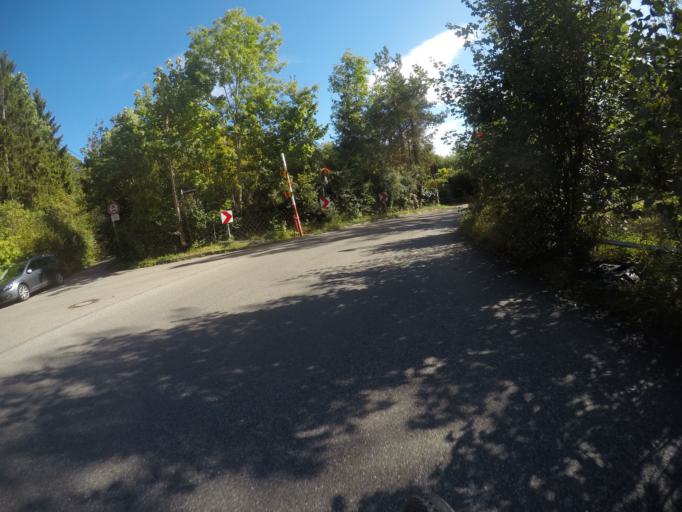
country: DE
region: Baden-Wuerttemberg
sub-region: Regierungsbezirk Stuttgart
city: Stuttgart-Ost
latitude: 48.7609
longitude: 9.2261
